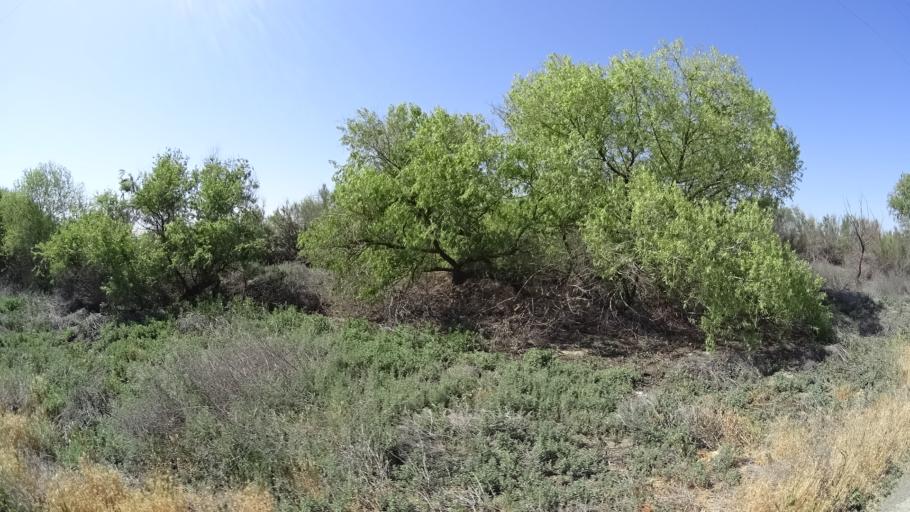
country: US
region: California
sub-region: Kings County
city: Corcoran
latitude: 36.0072
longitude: -119.5478
